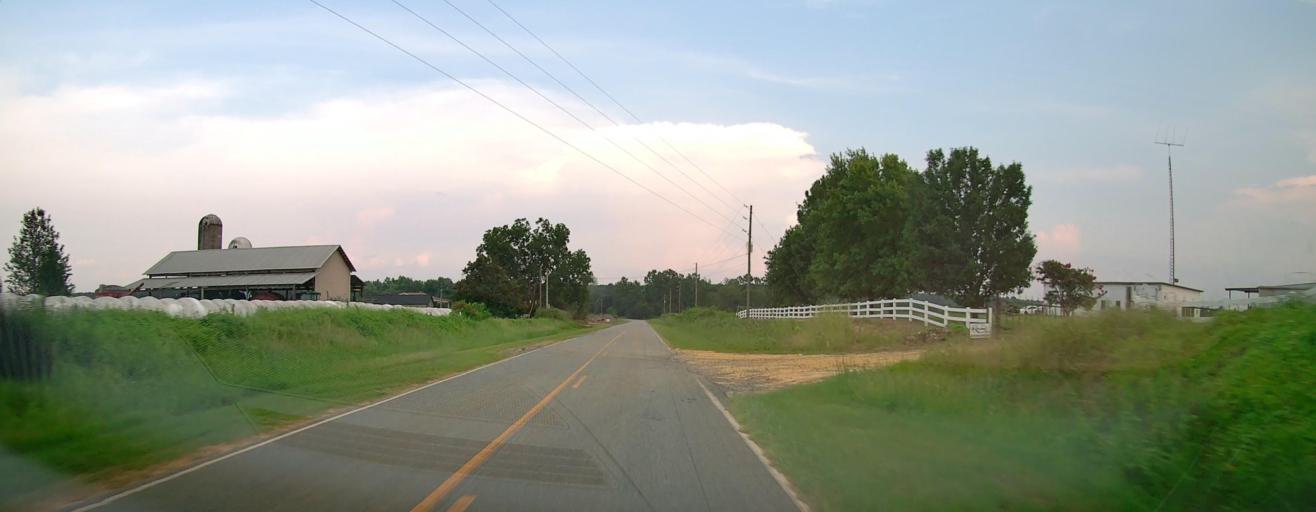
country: US
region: Georgia
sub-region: Laurens County
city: East Dublin
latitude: 32.6427
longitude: -82.8150
